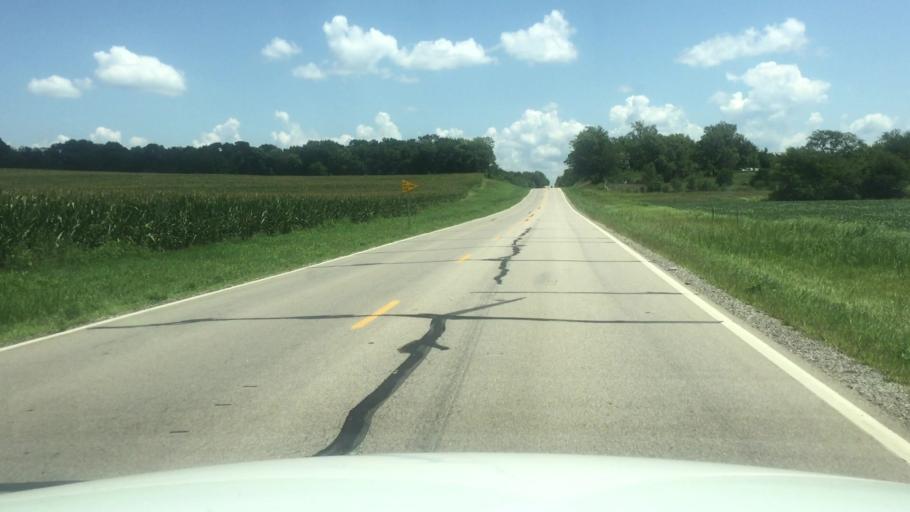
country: US
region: Kansas
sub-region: Brown County
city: Horton
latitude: 39.6673
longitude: -95.5454
